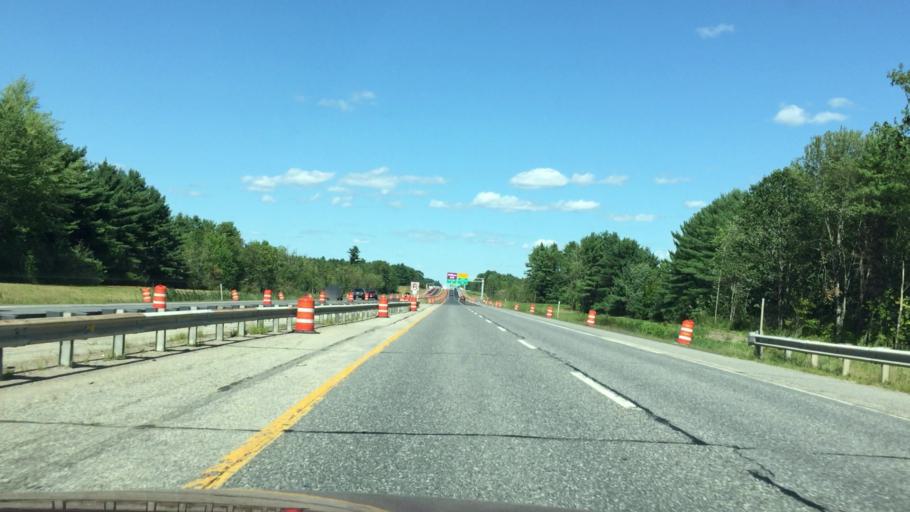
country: US
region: Maine
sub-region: Kennebec County
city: Gardiner
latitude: 44.1799
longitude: -69.8596
